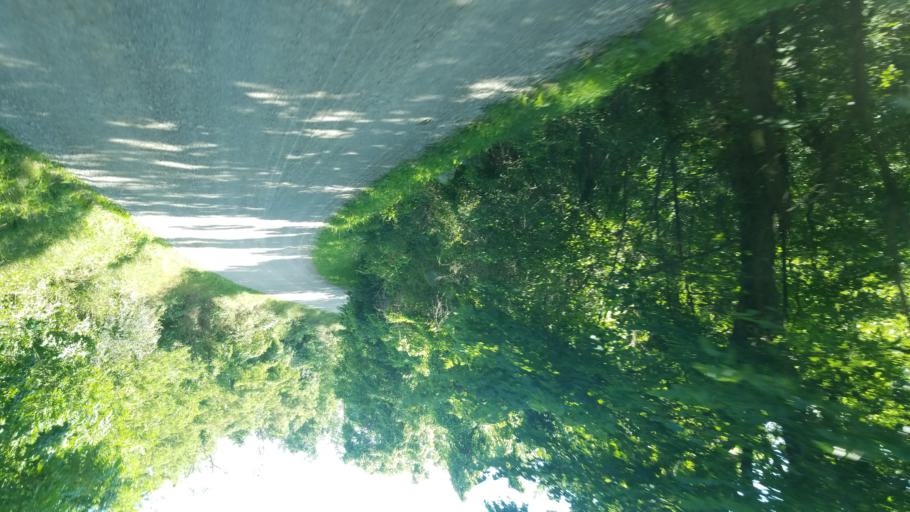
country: US
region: Ohio
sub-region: Gallia County
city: Gallipolis
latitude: 38.7439
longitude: -82.3478
